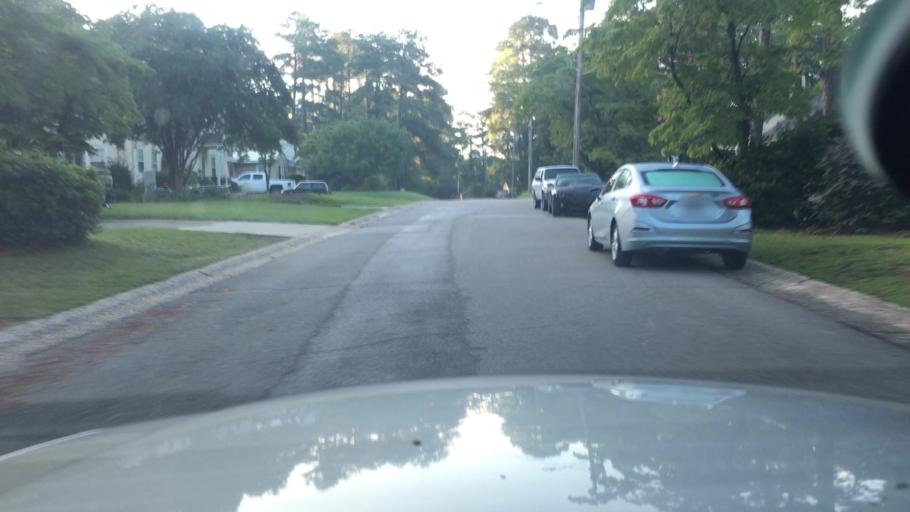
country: US
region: North Carolina
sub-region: Cumberland County
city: Fayetteville
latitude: 35.0624
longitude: -78.9153
